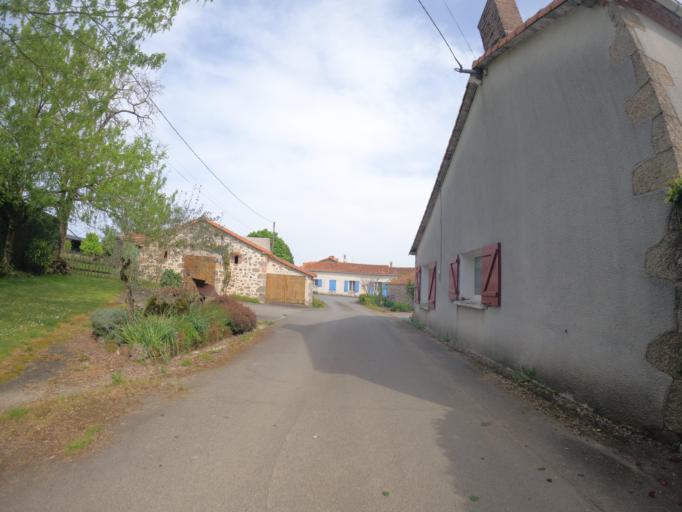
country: FR
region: Poitou-Charentes
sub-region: Departement des Deux-Sevres
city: La Chapelle-Saint-Laurent
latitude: 46.7055
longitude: -0.4984
